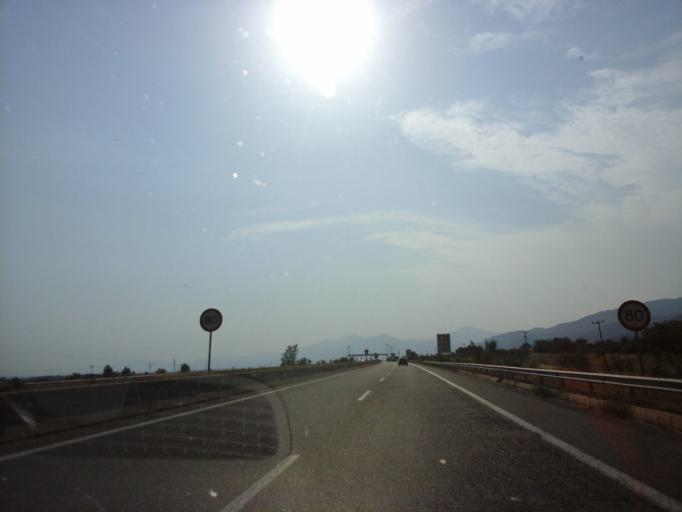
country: GR
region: East Macedonia and Thrace
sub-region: Nomos Xanthis
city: Selero
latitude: 41.1199
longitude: 25.0883
